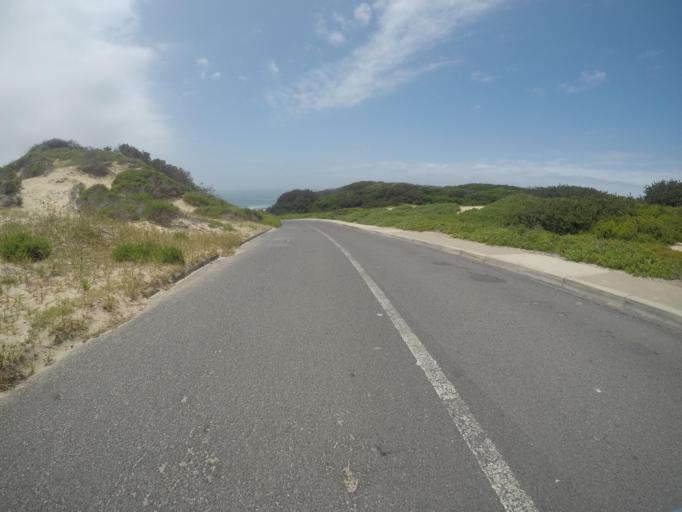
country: ZA
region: Eastern Cape
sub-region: Buffalo City Metropolitan Municipality
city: East London
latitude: -32.9964
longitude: 27.9505
